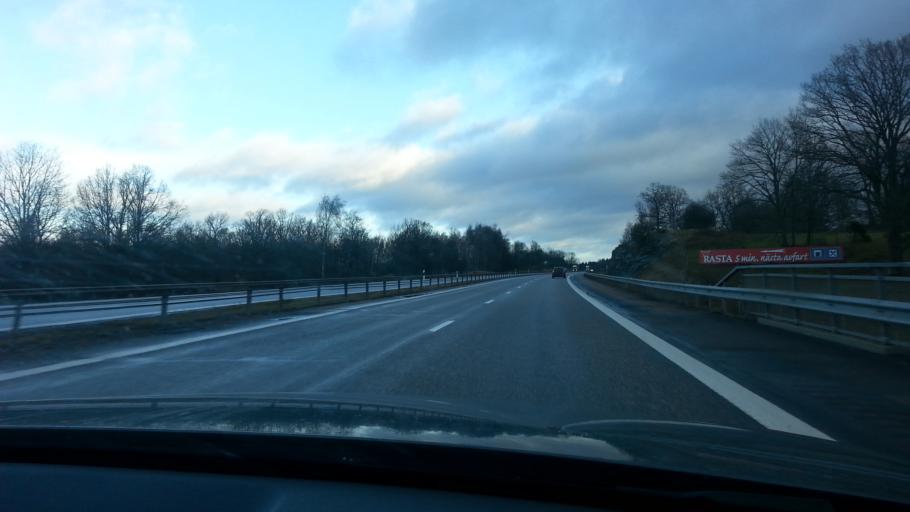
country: SE
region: OEstergoetland
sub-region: Odeshogs Kommun
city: OEdeshoeg
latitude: 58.1751
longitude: 14.5900
